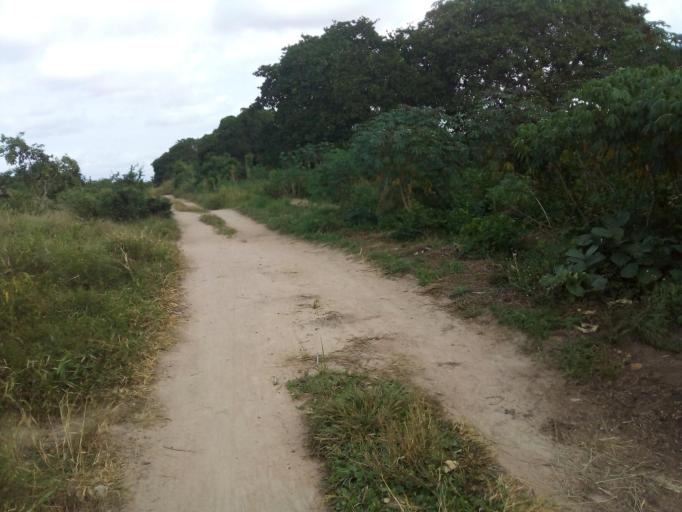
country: MZ
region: Zambezia
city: Quelimane
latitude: -17.5537
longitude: 36.7001
